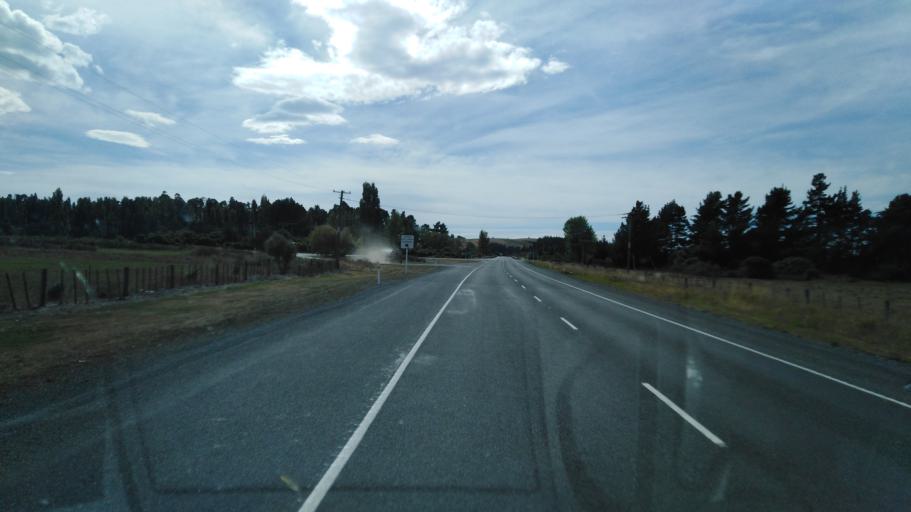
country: NZ
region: Canterbury
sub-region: Kaikoura District
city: Kaikoura
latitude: -42.4171
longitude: 173.6276
